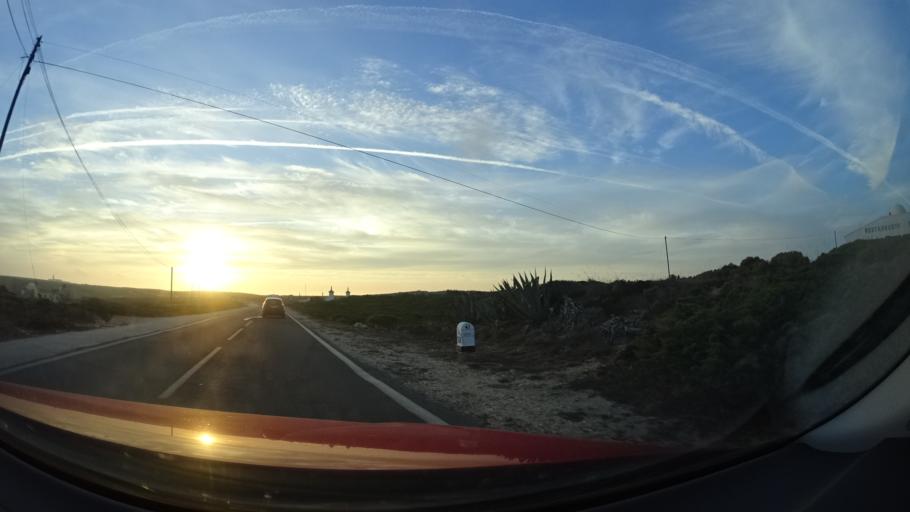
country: PT
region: Faro
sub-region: Vila do Bispo
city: Sagres
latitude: 37.0280
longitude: -8.9800
